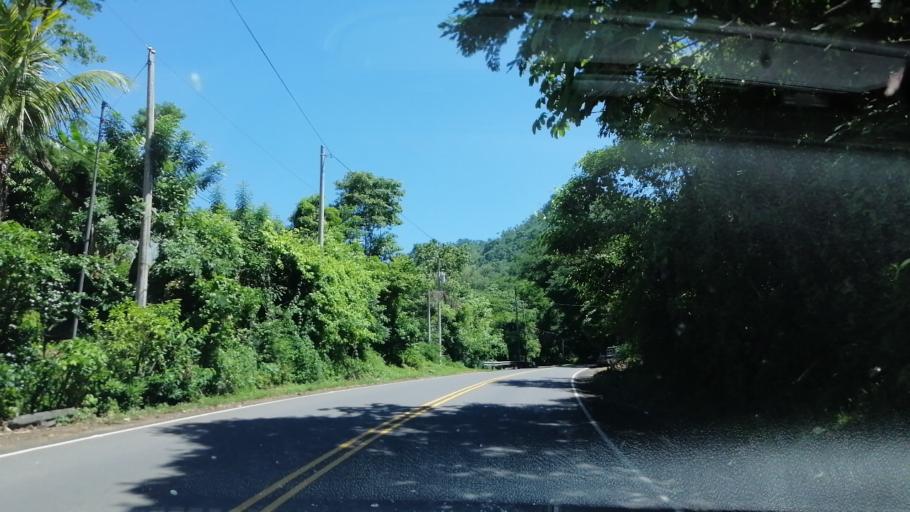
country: SV
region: Morazan
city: Cacaopera
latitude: 13.7959
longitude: -88.1472
